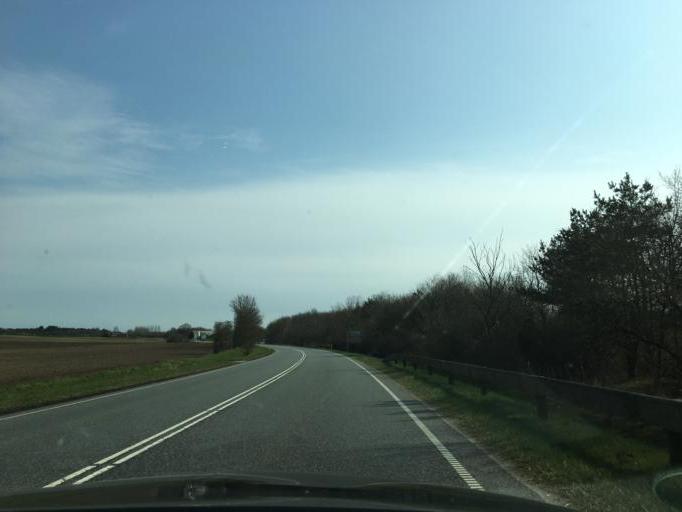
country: DK
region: South Denmark
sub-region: Kolding Kommune
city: Lunderskov
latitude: 55.4846
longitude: 9.2808
